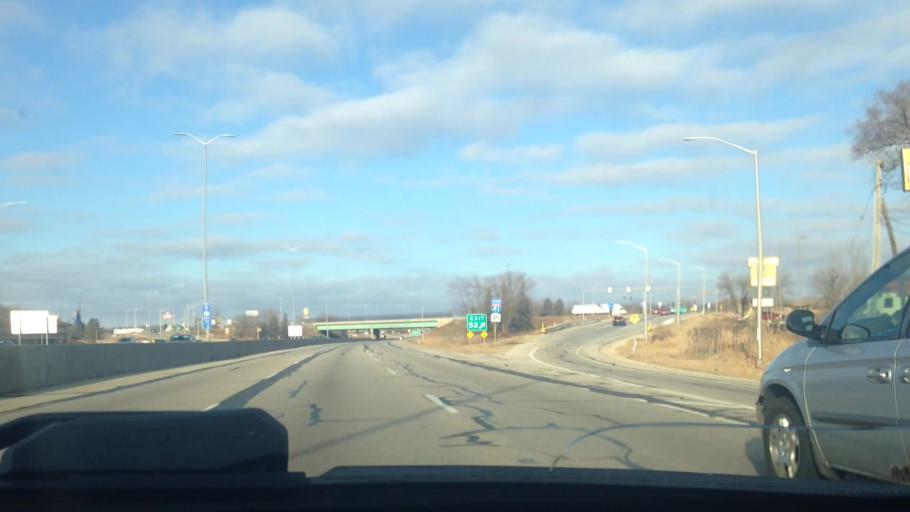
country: US
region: Wisconsin
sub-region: Waukesha County
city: Menomonee Falls
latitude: 43.1901
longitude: -88.1183
